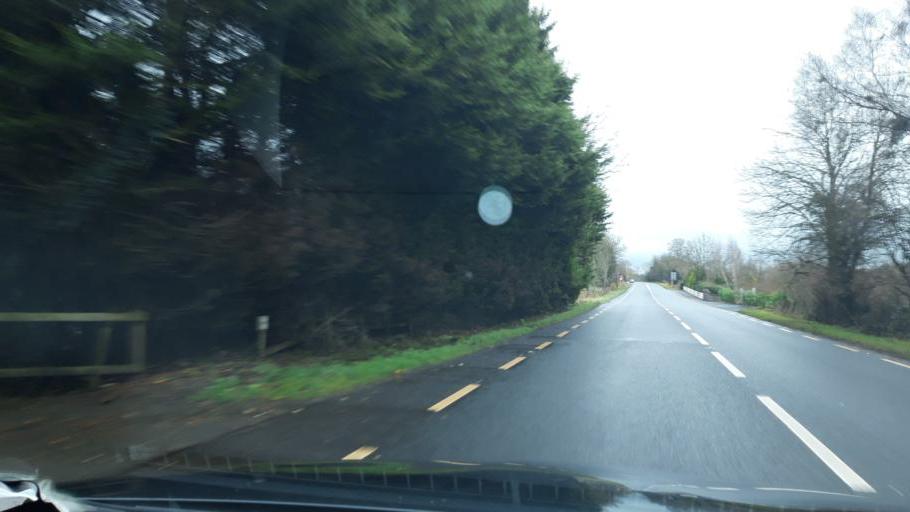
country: IE
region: Ulster
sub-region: County Monaghan
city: Castleblayney
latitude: 54.0966
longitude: -6.7039
